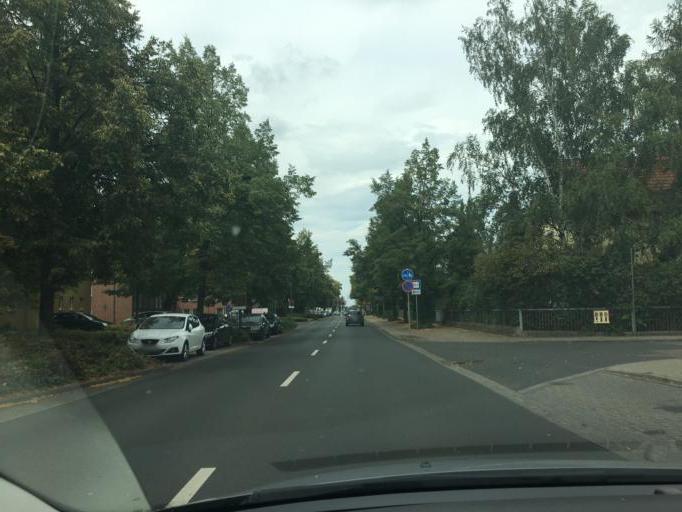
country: DE
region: Saxony-Anhalt
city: Merseburg
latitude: 51.3703
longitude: 11.9895
